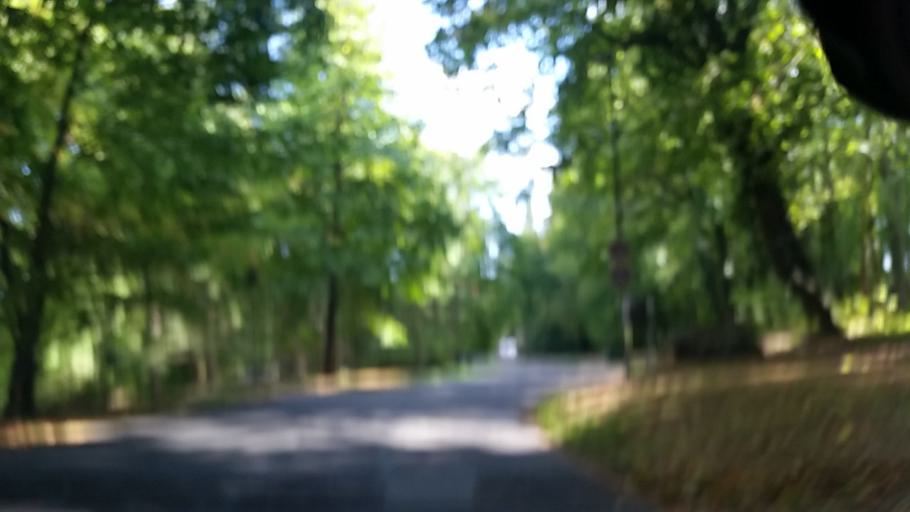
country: DE
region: Hesse
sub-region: Regierungsbezirk Kassel
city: Baunatal
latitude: 51.3127
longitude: 9.4206
